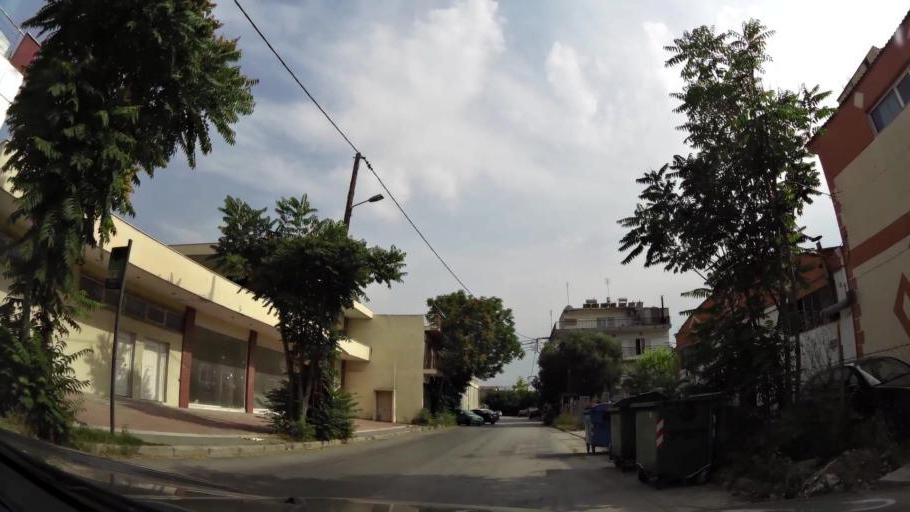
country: GR
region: Central Macedonia
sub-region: Nomos Thessalonikis
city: Stavroupoli
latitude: 40.6797
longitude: 22.9365
